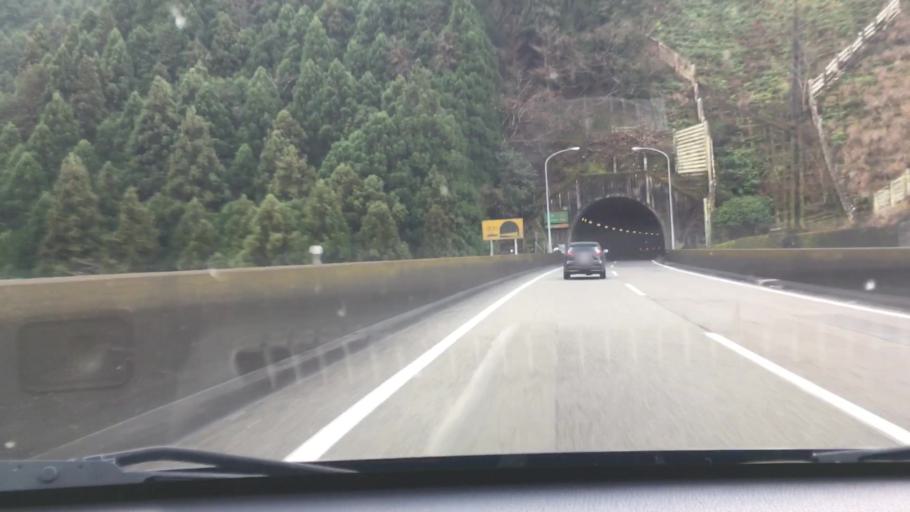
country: JP
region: Kumamoto
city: Yatsushiro
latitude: 32.4248
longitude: 130.7020
